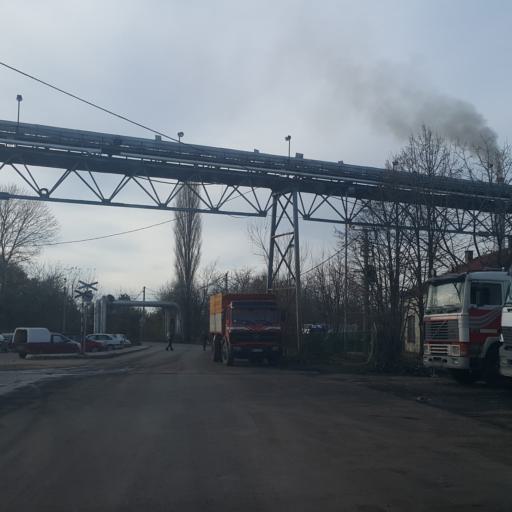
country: RS
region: Central Serbia
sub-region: Belgrade
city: Lazarevac
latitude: 44.4294
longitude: 20.2840
